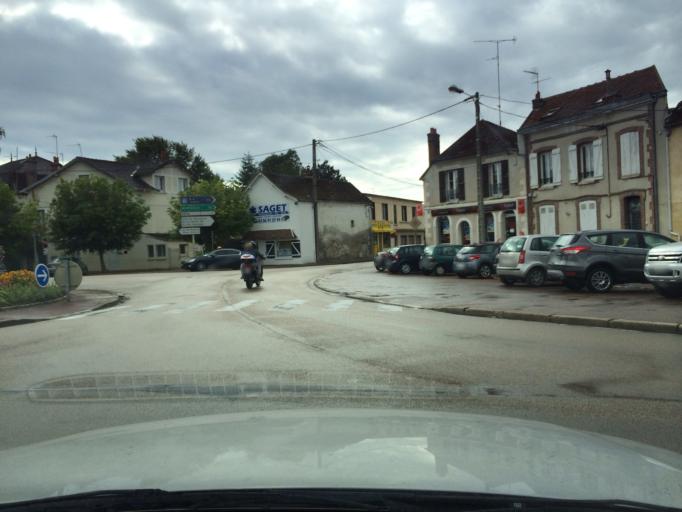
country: FR
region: Bourgogne
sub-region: Departement de l'Yonne
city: Joigny
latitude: 47.9773
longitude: 3.3942
